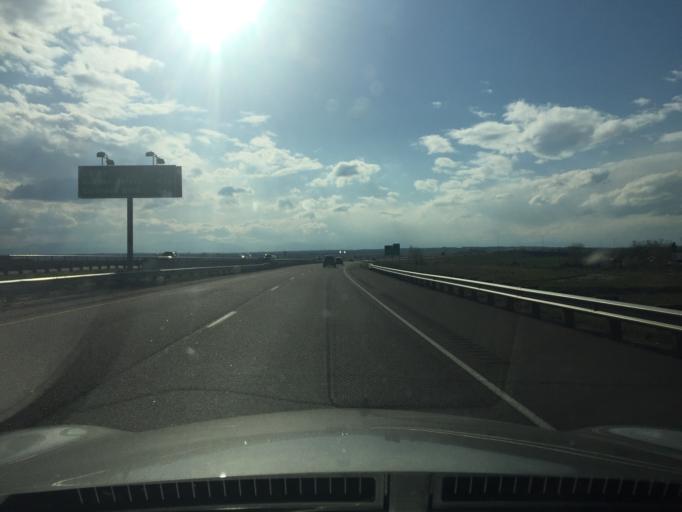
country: US
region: Colorado
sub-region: Adams County
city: Brighton
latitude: 39.9286
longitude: -104.8325
